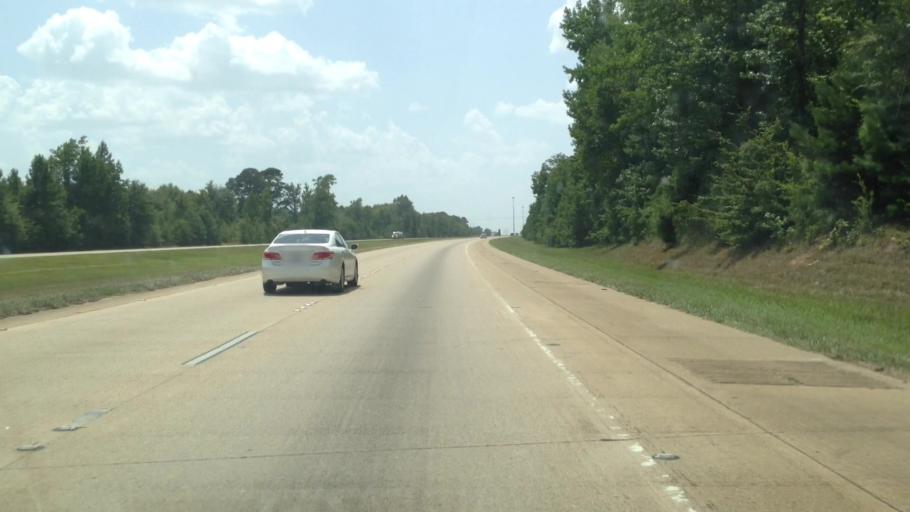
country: US
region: Louisiana
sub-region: Lincoln Parish
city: Grambling
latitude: 32.5406
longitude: -92.6990
